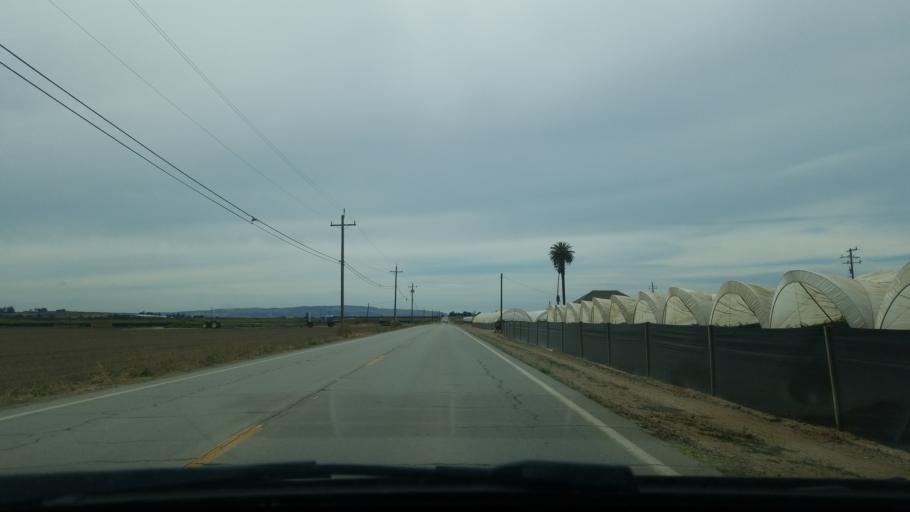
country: US
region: California
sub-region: Santa Barbara County
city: Santa Maria
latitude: 34.9233
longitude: -120.3628
